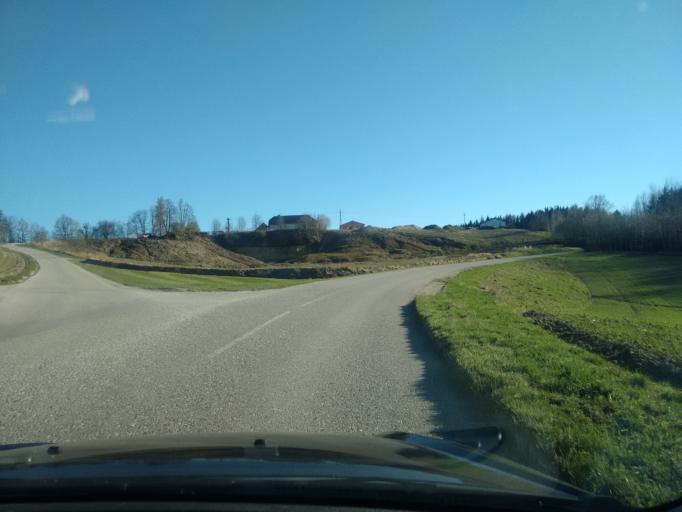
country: AT
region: Upper Austria
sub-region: Wels-Land
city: Offenhausen
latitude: 48.1677
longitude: 13.8591
